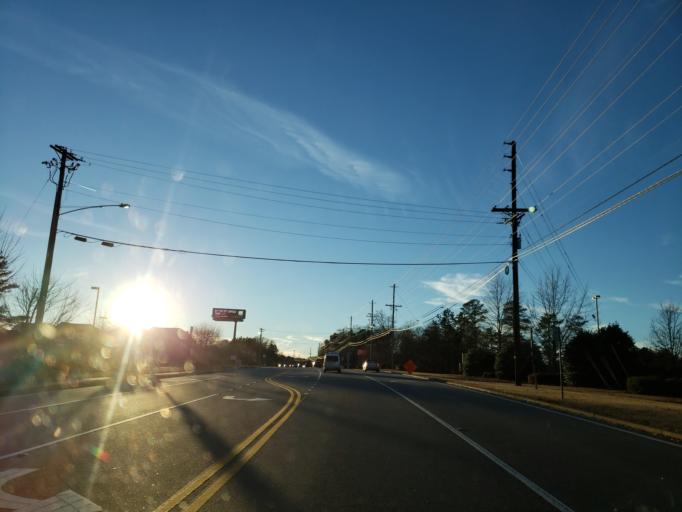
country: US
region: Georgia
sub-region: Fulton County
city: Alpharetta
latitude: 34.0921
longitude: -84.2882
